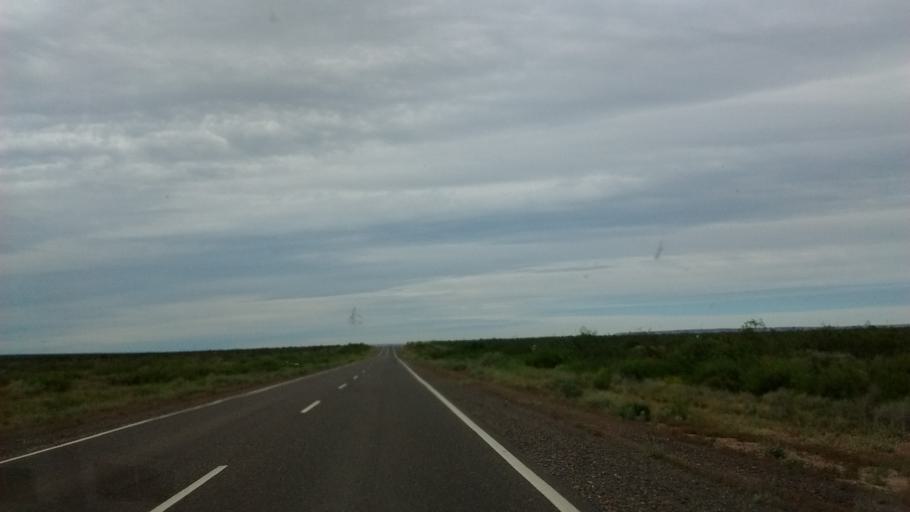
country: AR
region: Rio Negro
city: Catriel
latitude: -38.0578
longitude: -67.9209
